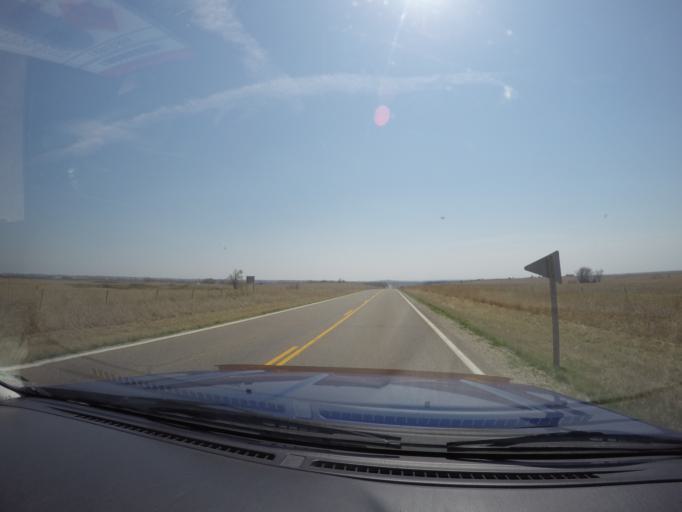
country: US
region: Kansas
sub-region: Morris County
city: Council Grove
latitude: 38.7531
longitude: -96.5012
